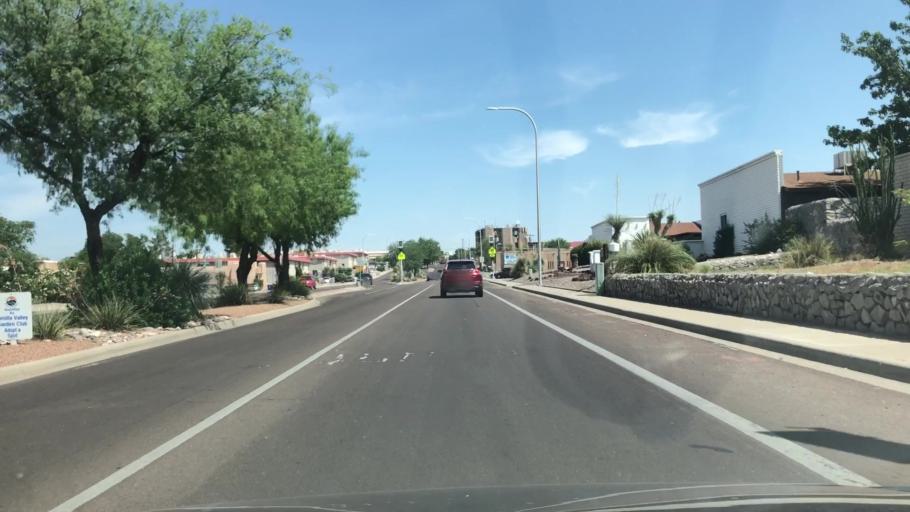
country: US
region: New Mexico
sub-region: Dona Ana County
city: University Park
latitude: 32.3021
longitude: -106.7373
